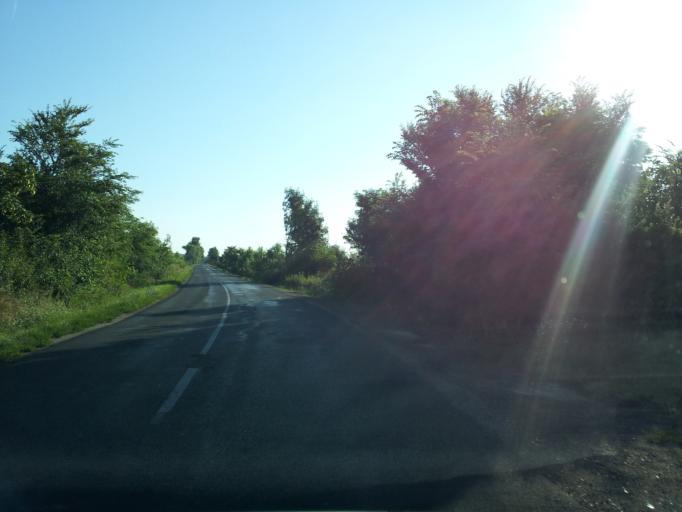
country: HU
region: Fejer
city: Lepseny
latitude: 47.0329
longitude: 18.2251
